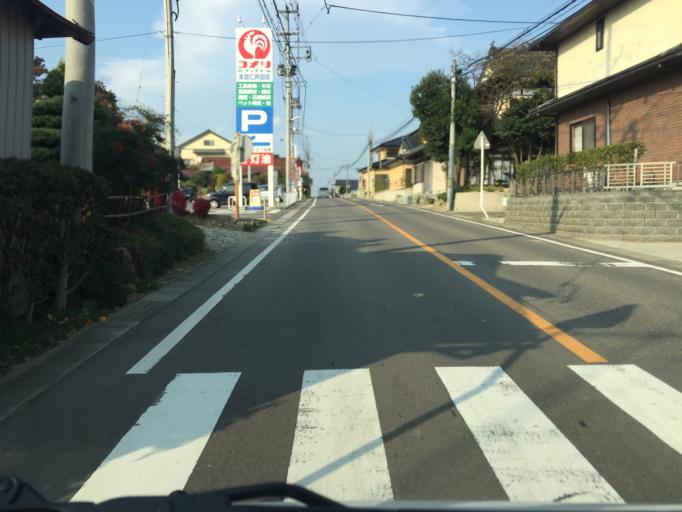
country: JP
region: Fukushima
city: Motomiya
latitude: 37.4925
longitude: 140.4012
